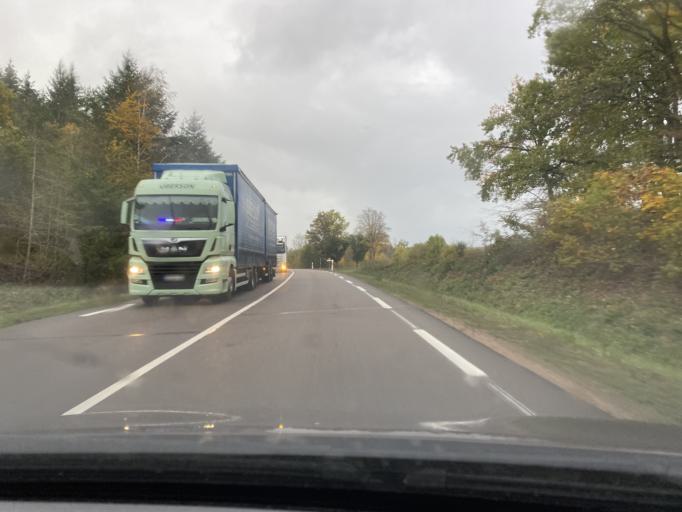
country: FR
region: Bourgogne
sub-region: Departement de la Cote-d'Or
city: Saulieu
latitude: 47.3077
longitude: 4.2079
